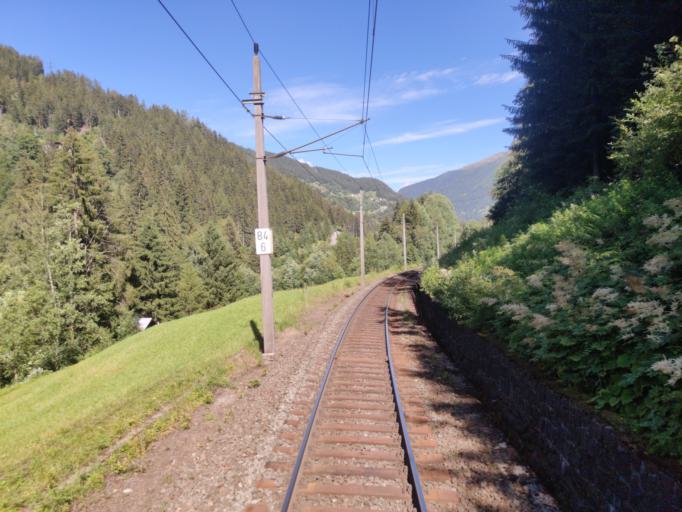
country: AT
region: Tyrol
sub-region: Politischer Bezirk Landeck
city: Strengen
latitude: 47.1294
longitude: 10.4391
